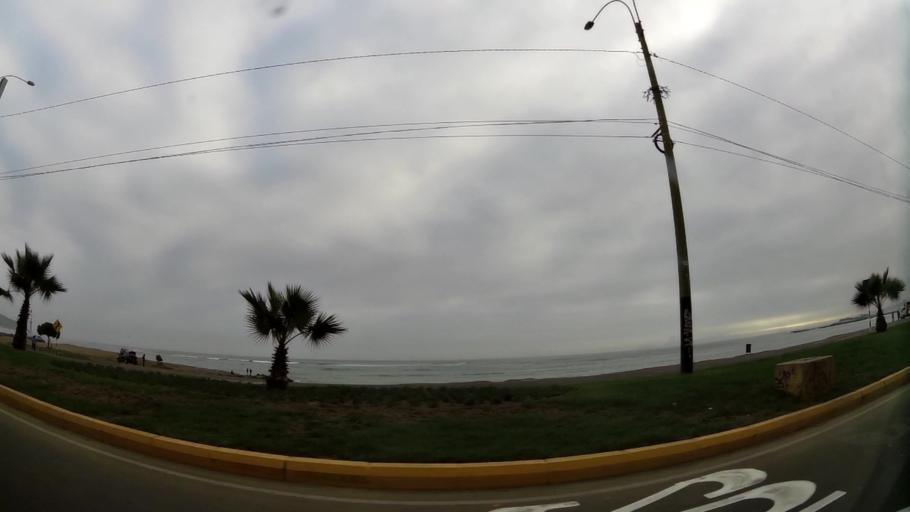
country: PE
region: Lima
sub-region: Lima
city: Surco
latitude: -12.1368
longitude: -77.0285
